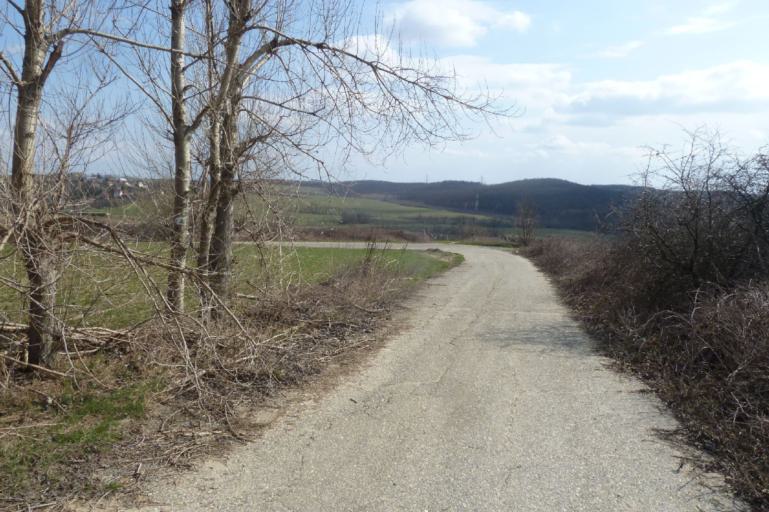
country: HU
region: Pest
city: Mogyorod
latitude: 47.5913
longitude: 19.2691
